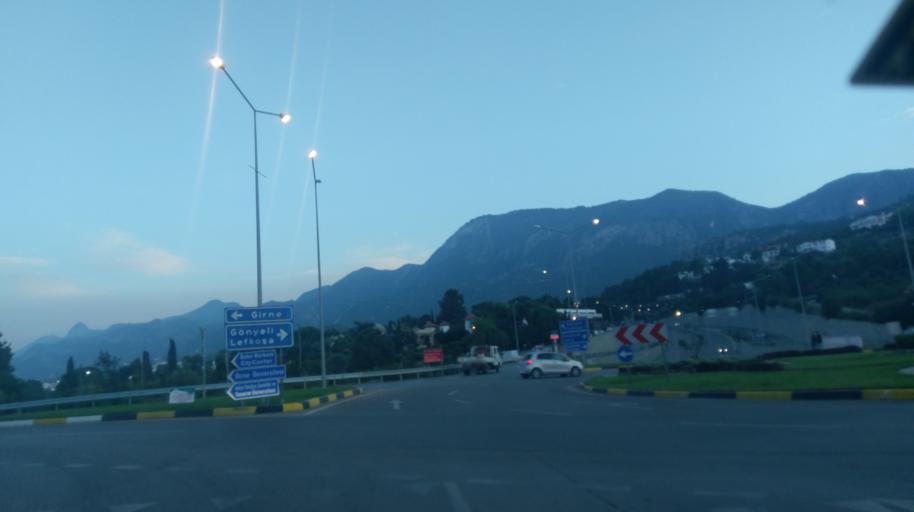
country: CY
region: Keryneia
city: Kyrenia
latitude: 35.3258
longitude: 33.3176
